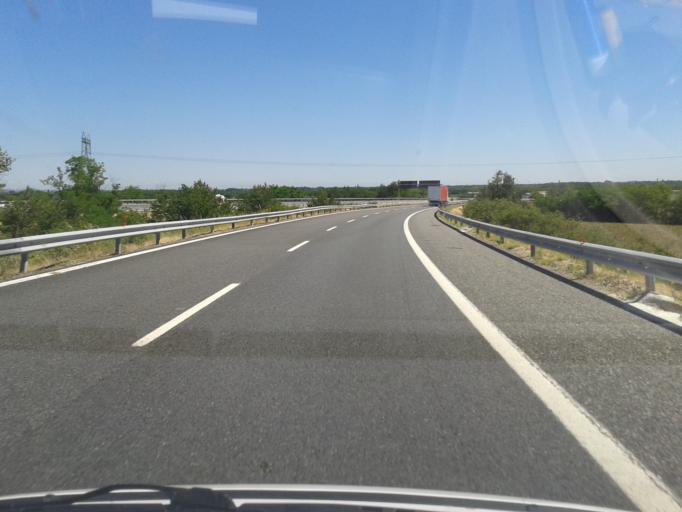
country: IT
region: Piedmont
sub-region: Provincia di Alessandria
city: Predosa
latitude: 44.7621
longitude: 8.6465
